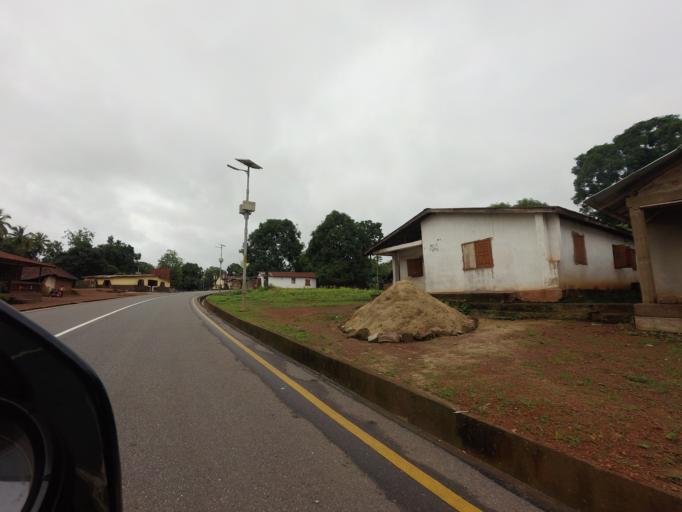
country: SL
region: Northern Province
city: Kambia
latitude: 9.1268
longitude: -12.9191
